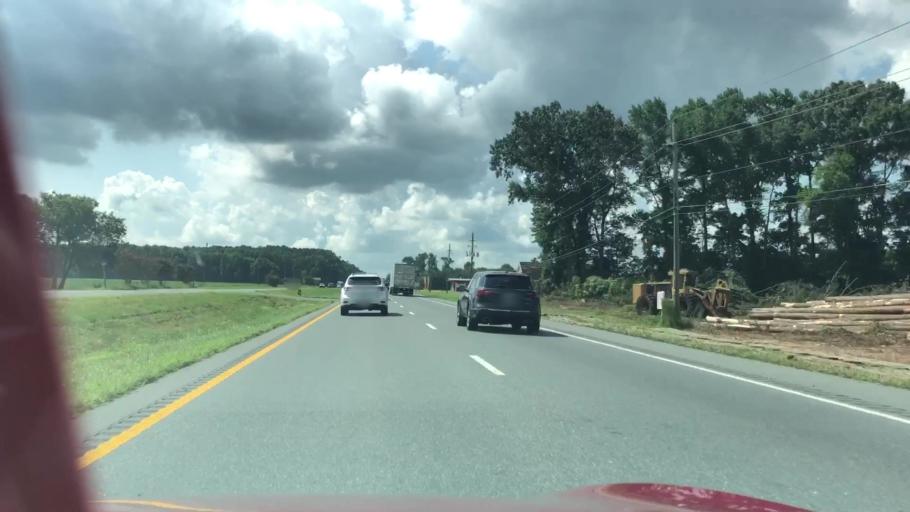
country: US
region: Virginia
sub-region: Accomack County
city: Wattsville
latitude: 37.9107
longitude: -75.5493
